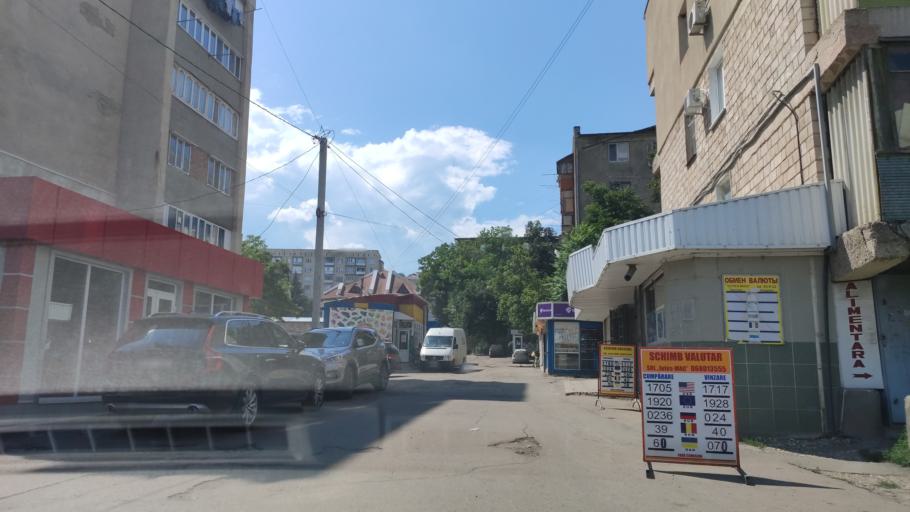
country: MD
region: Raionul Soroca
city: Soroca
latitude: 48.1602
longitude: 28.3030
